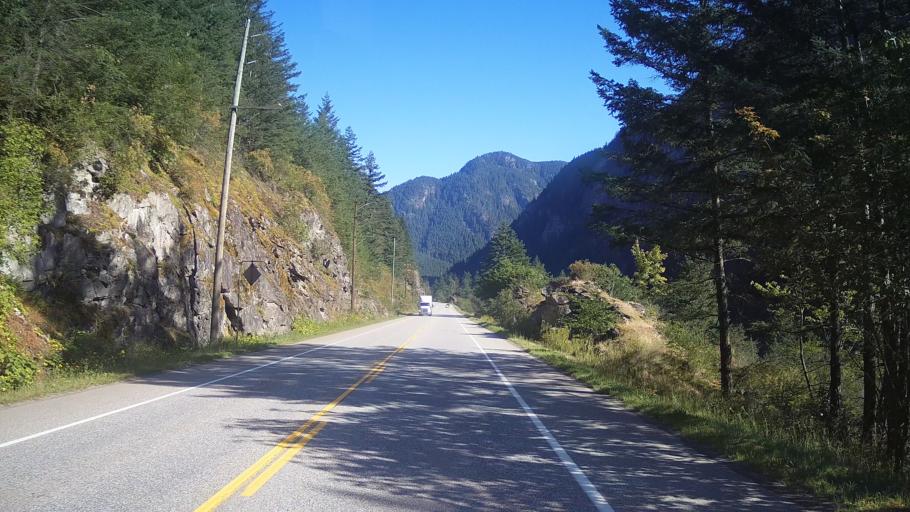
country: CA
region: British Columbia
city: Hope
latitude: 49.5822
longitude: -121.4031
